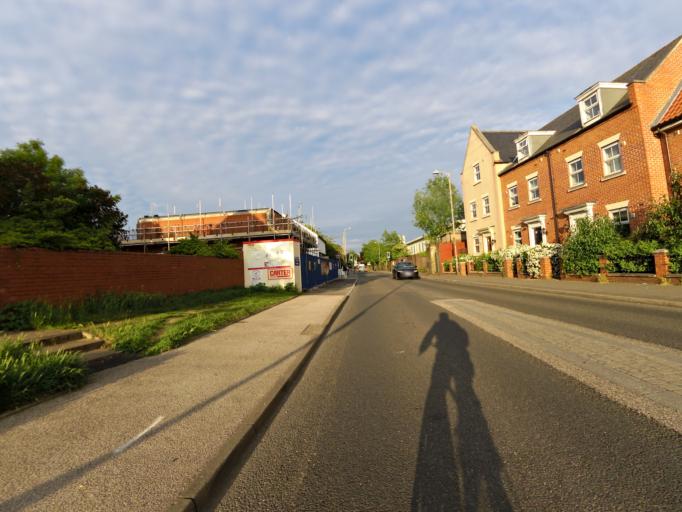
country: GB
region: England
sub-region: Suffolk
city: Ipswich
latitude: 52.0579
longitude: 1.1394
